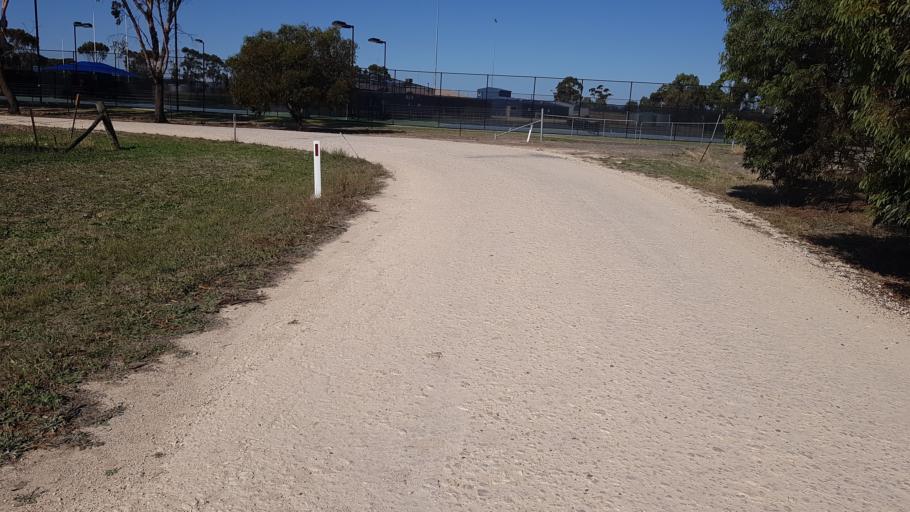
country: AU
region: Victoria
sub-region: Horsham
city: Horsham
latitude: -36.7434
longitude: 141.9470
